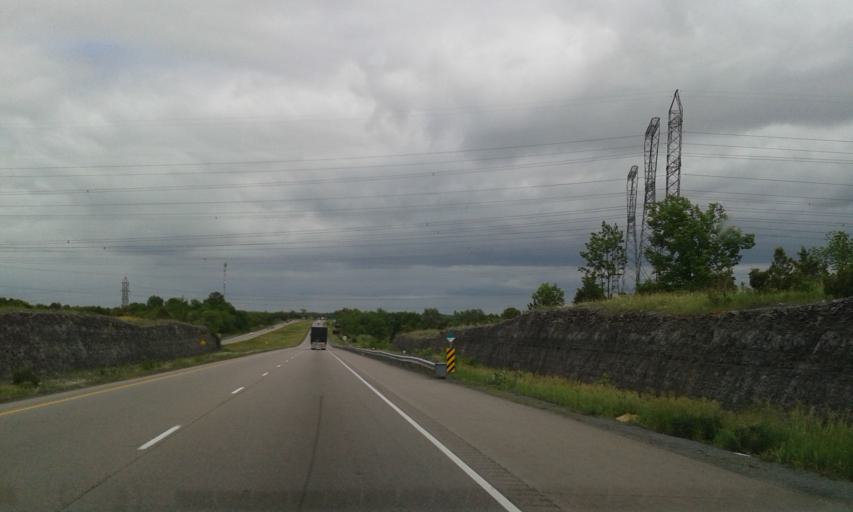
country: CA
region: Ontario
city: Kingston
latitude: 44.2859
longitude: -76.6469
